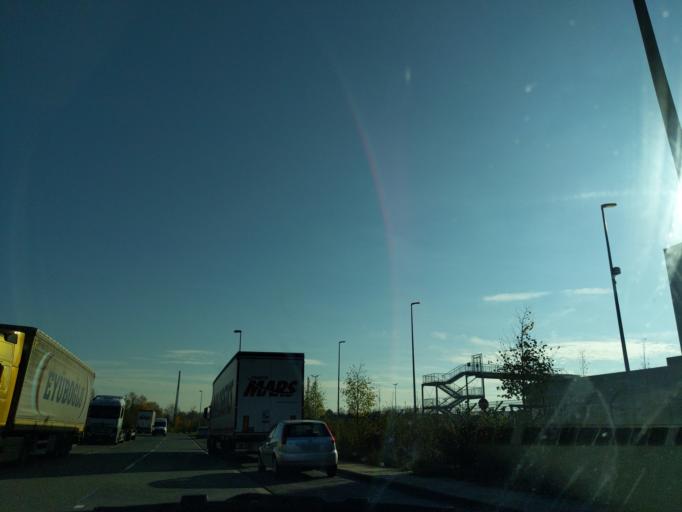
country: DE
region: North Rhine-Westphalia
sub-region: Regierungsbezirk Koln
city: Bilderstoeckchen
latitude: 51.0118
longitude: 6.9306
